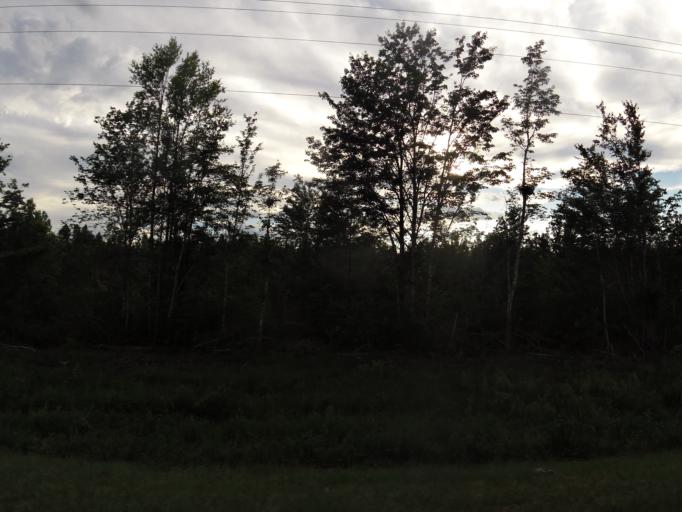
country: US
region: South Carolina
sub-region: Jasper County
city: Hardeeville
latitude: 32.3046
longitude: -81.0872
